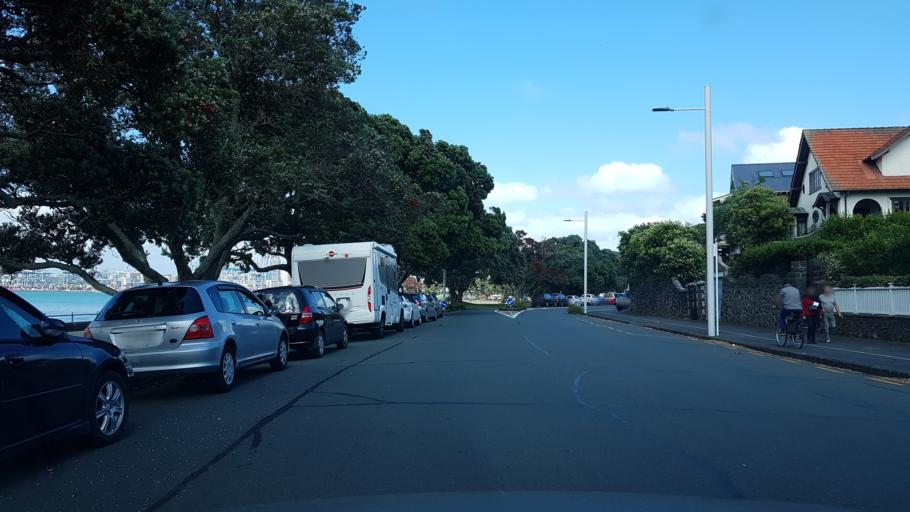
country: NZ
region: Auckland
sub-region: Auckland
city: Auckland
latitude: -36.8315
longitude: 174.8010
